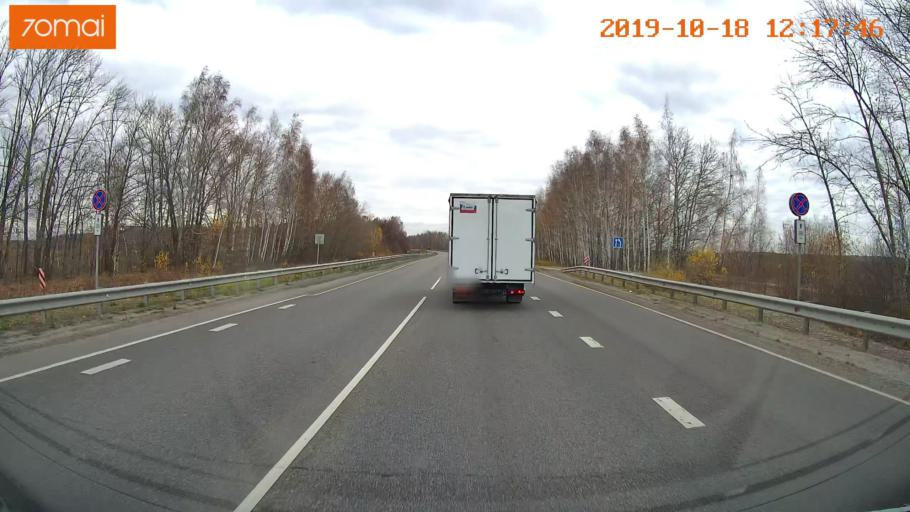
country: RU
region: Rjazan
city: Zakharovo
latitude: 54.4599
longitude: 39.4484
